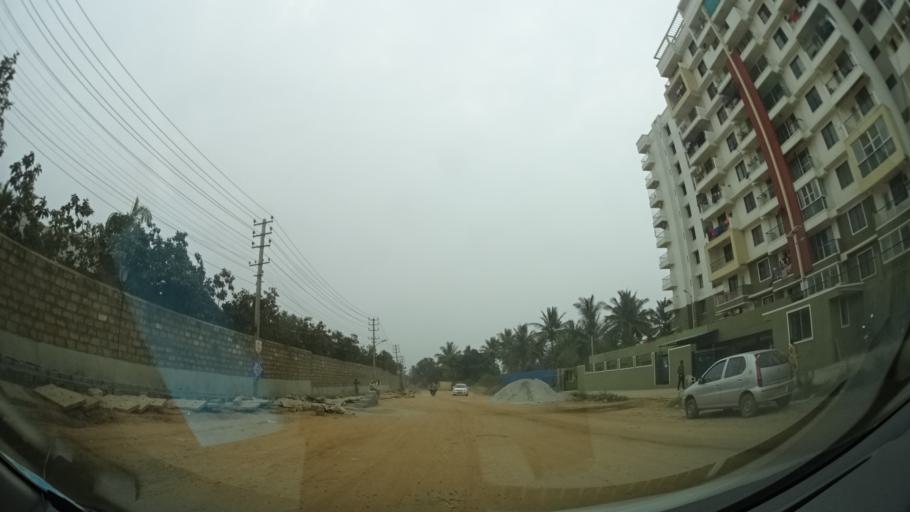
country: IN
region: Karnataka
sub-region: Bangalore Rural
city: Hoskote
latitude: 12.9683
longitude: 77.7428
